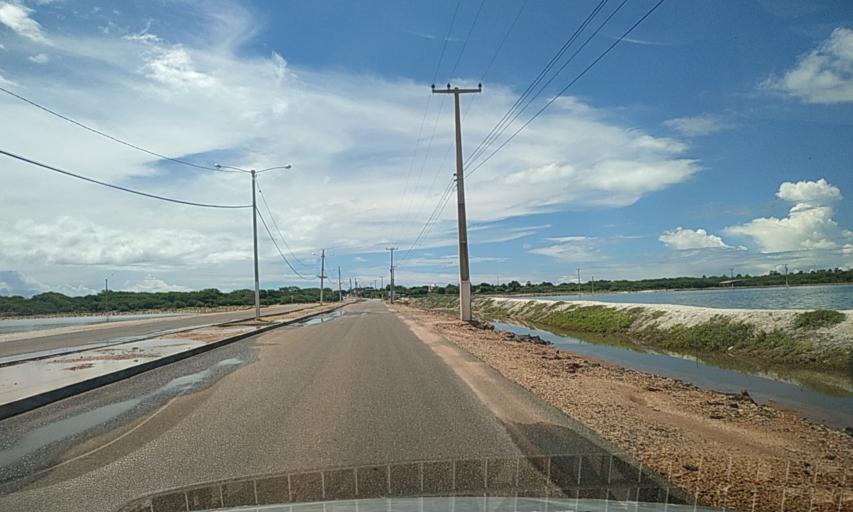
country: BR
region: Rio Grande do Norte
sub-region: Areia Branca
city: Areia Branca
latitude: -4.9369
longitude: -37.1133
